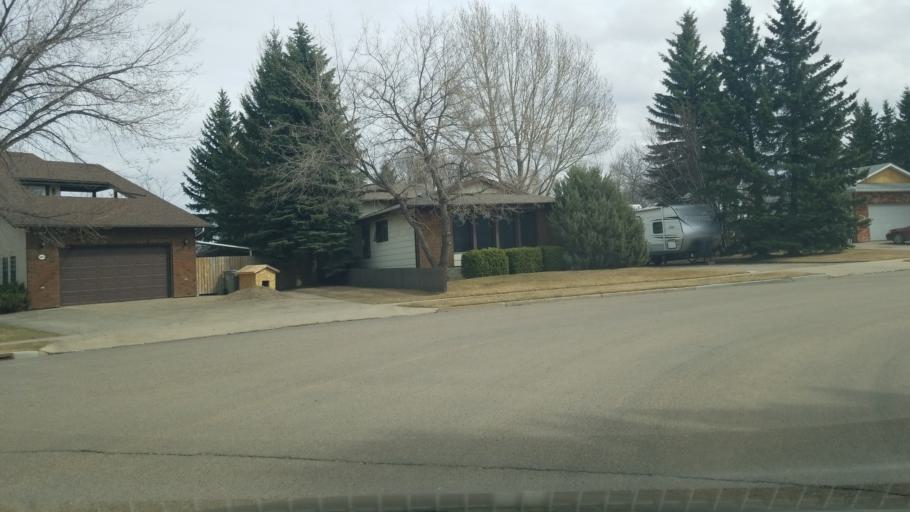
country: CA
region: Saskatchewan
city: Lloydminster
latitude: 53.2700
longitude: -110.0260
